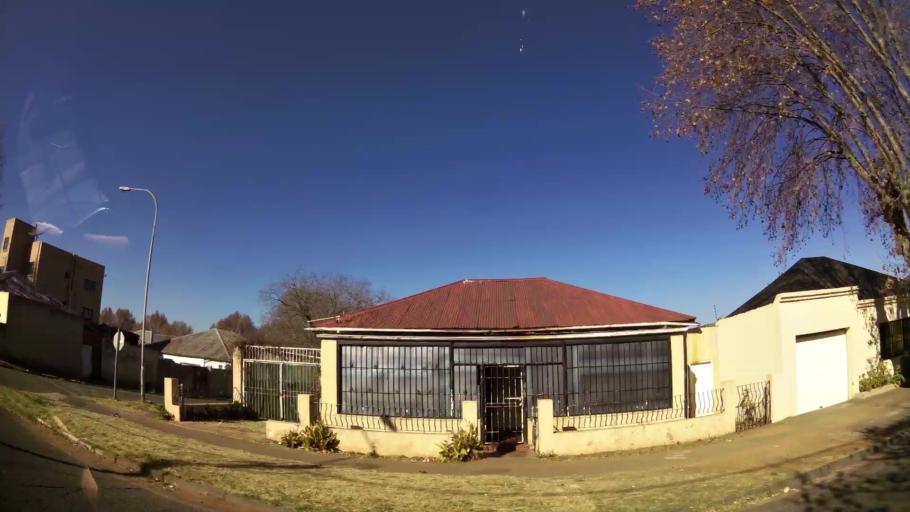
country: ZA
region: Gauteng
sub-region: City of Johannesburg Metropolitan Municipality
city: Johannesburg
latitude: -26.2027
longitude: 28.0099
